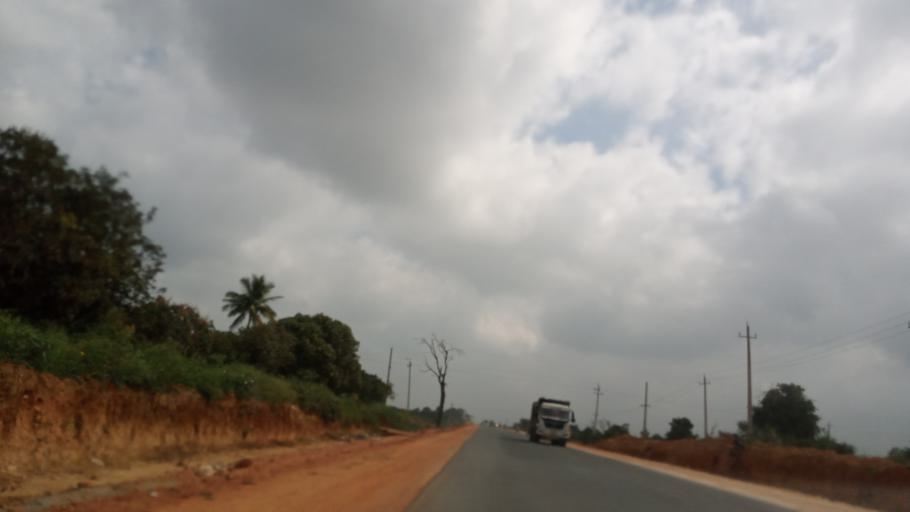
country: IN
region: Karnataka
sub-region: Kolar
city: Srinivaspur
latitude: 13.4459
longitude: 78.2379
